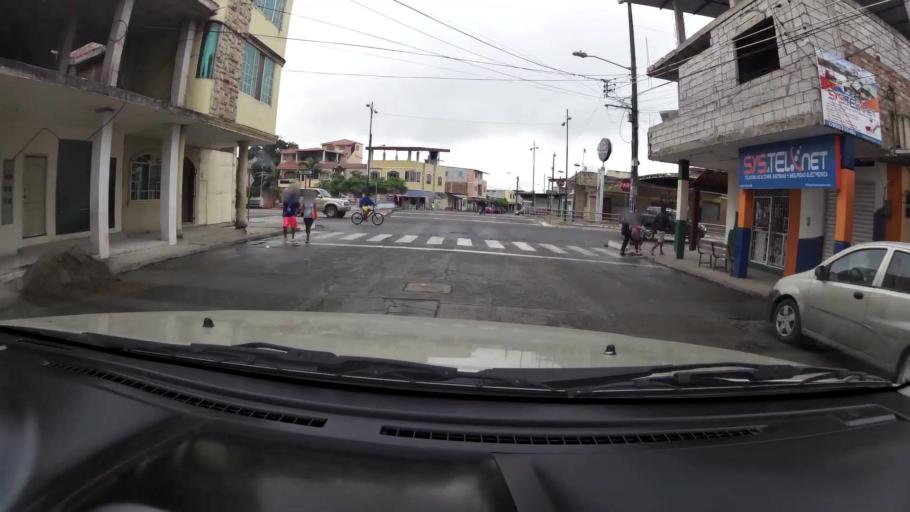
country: EC
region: El Oro
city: Pasaje
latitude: -3.3301
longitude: -79.8056
